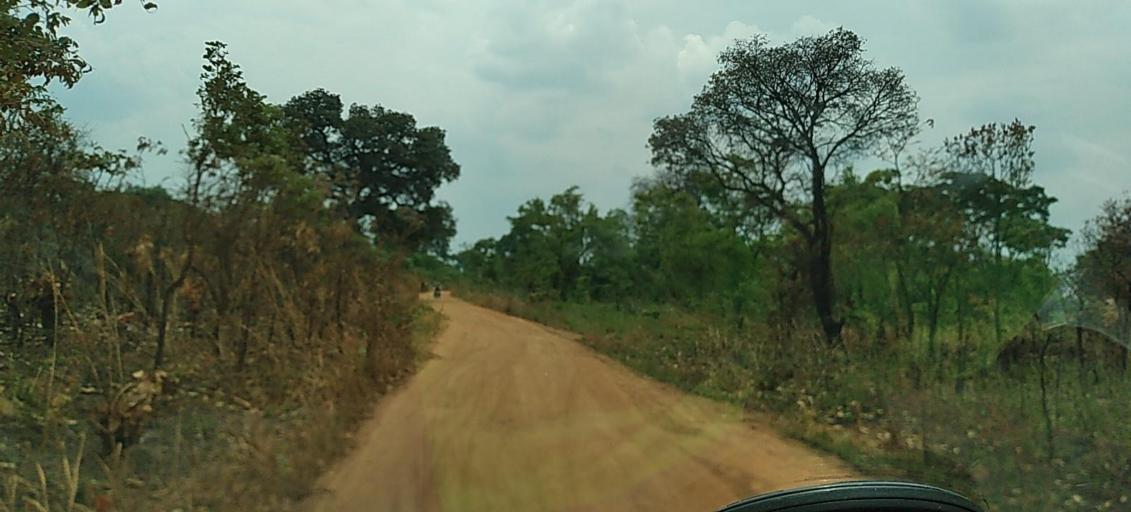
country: ZM
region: North-Western
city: Kansanshi
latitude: -12.0729
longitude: 26.3552
